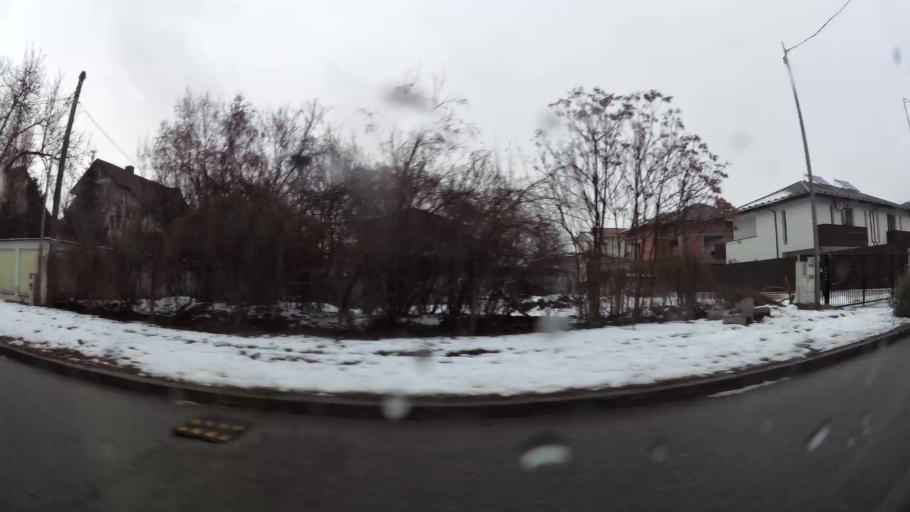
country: RO
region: Ilfov
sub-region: Comuna Mogosoaia
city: Mogosoaia
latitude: 44.4963
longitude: 26.0420
